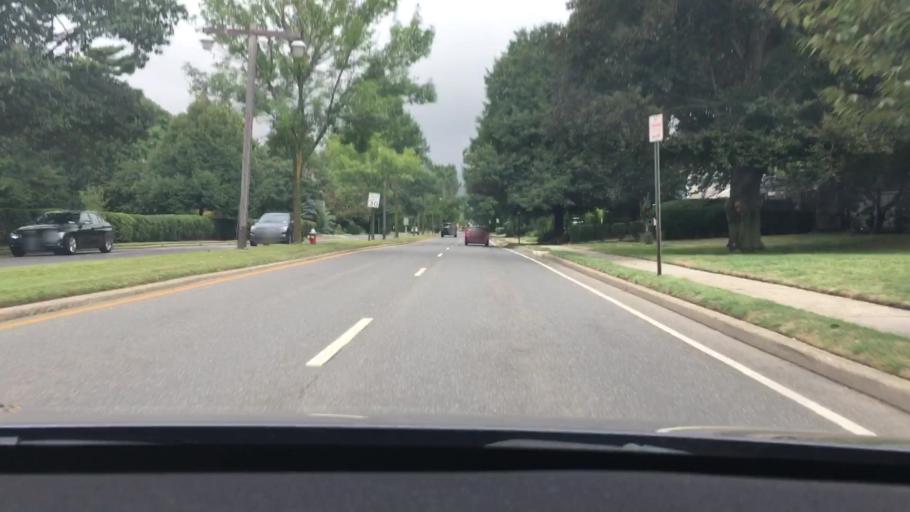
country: US
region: New York
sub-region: Nassau County
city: Garden City Park
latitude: 40.7296
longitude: -73.6607
